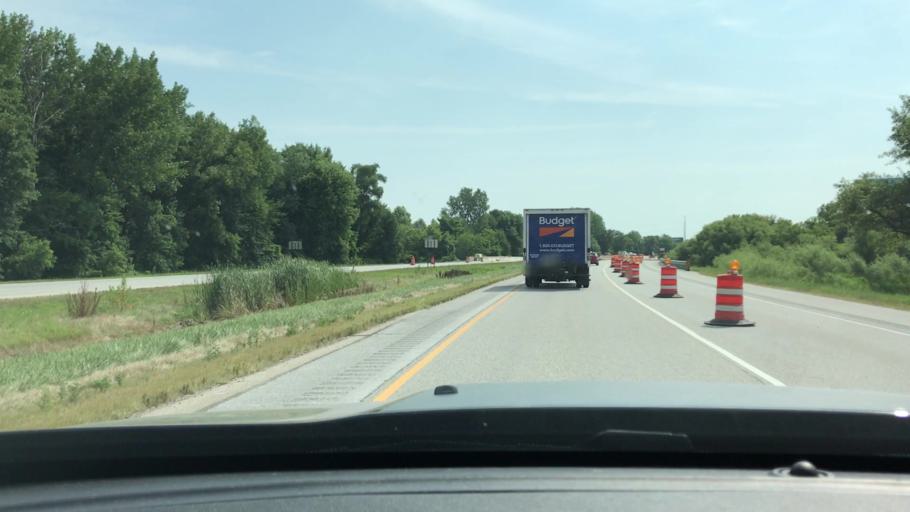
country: US
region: Illinois
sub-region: Rock Island County
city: Carbon Cliff
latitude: 41.4629
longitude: -90.3929
